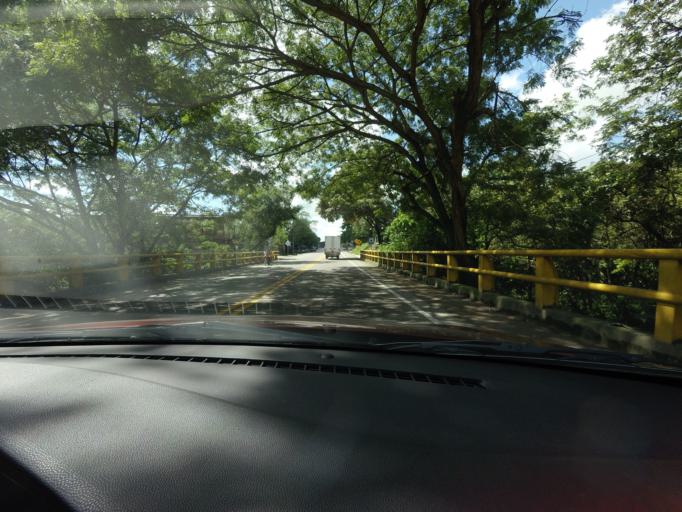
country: CO
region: Tolima
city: Saldana
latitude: 3.9374
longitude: -75.0185
